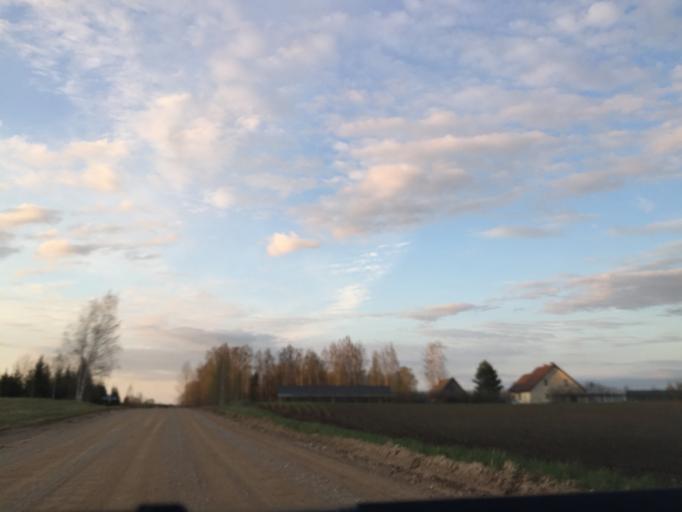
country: LV
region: Gulbenes Rajons
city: Gulbene
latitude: 57.2073
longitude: 26.7805
